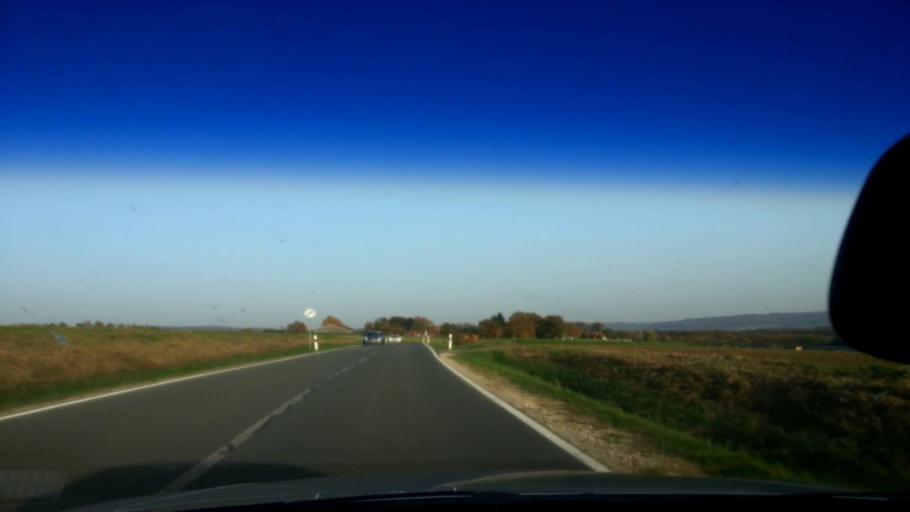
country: DE
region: Bavaria
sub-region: Upper Franconia
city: Zapfendorf
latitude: 49.9852
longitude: 10.9567
